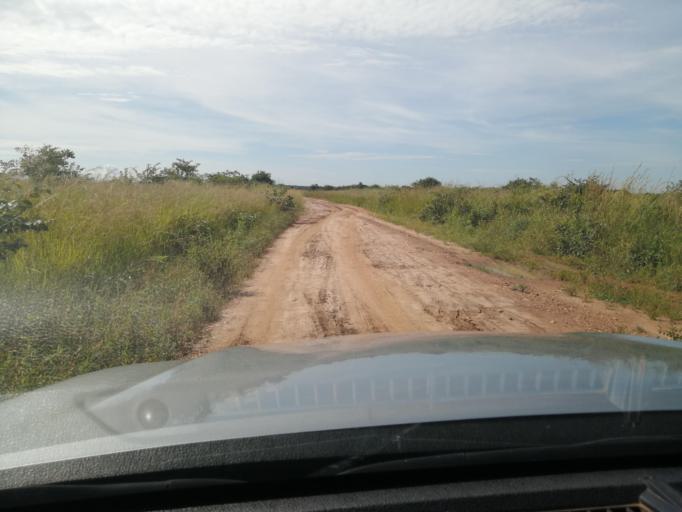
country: ZM
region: Central
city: Chibombo
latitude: -14.9357
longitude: 27.7915
